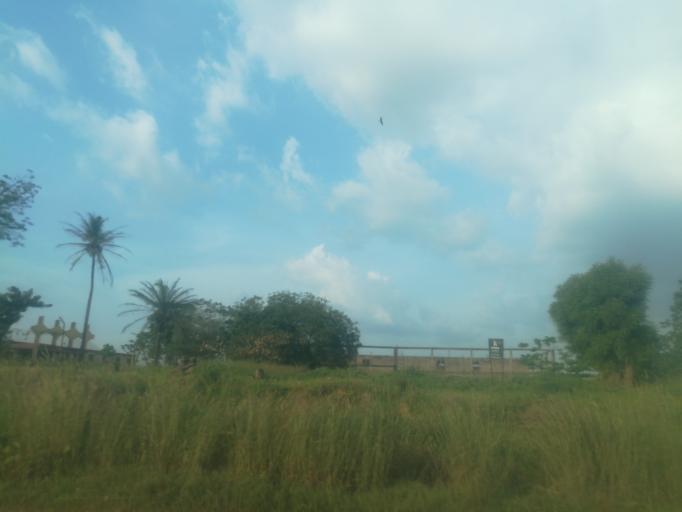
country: NG
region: Ogun
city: Abeokuta
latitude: 7.1691
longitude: 3.2964
